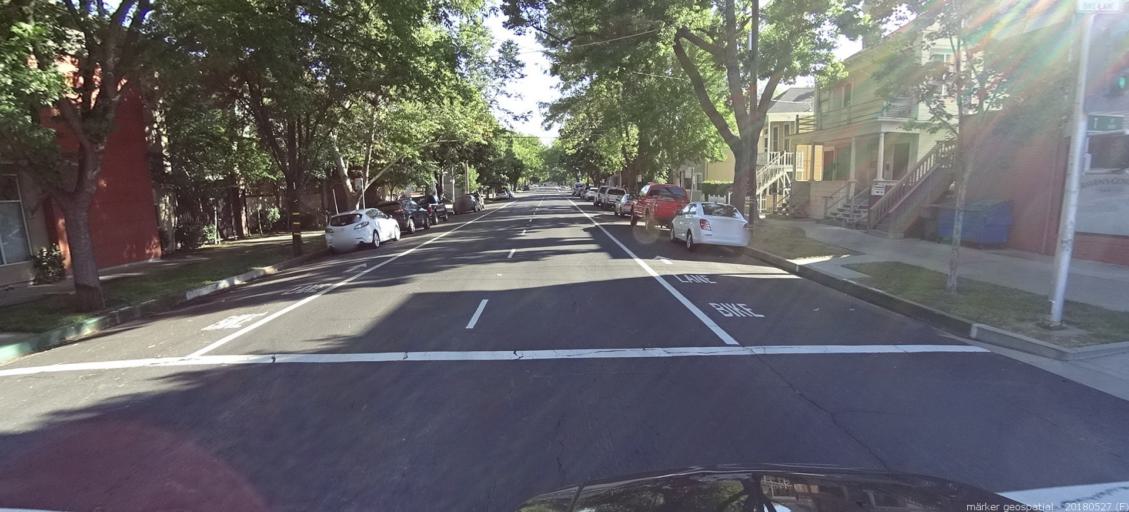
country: US
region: California
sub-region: Sacramento County
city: Sacramento
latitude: 38.5693
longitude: -121.4982
